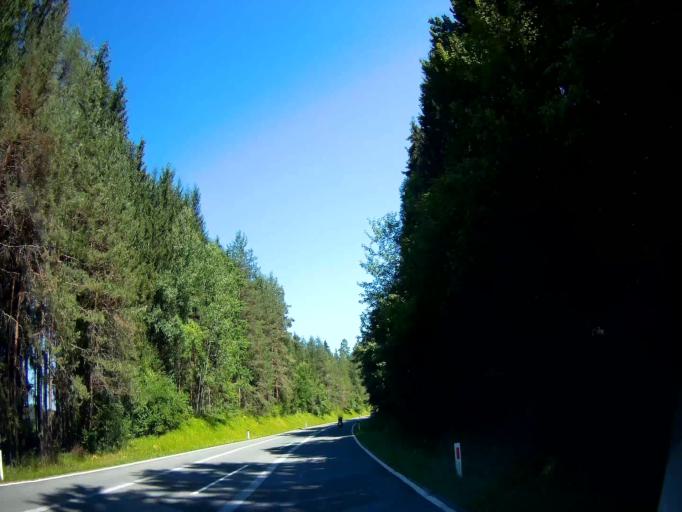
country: AT
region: Carinthia
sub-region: Politischer Bezirk Volkermarkt
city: Gallizien
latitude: 46.5511
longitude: 14.5092
